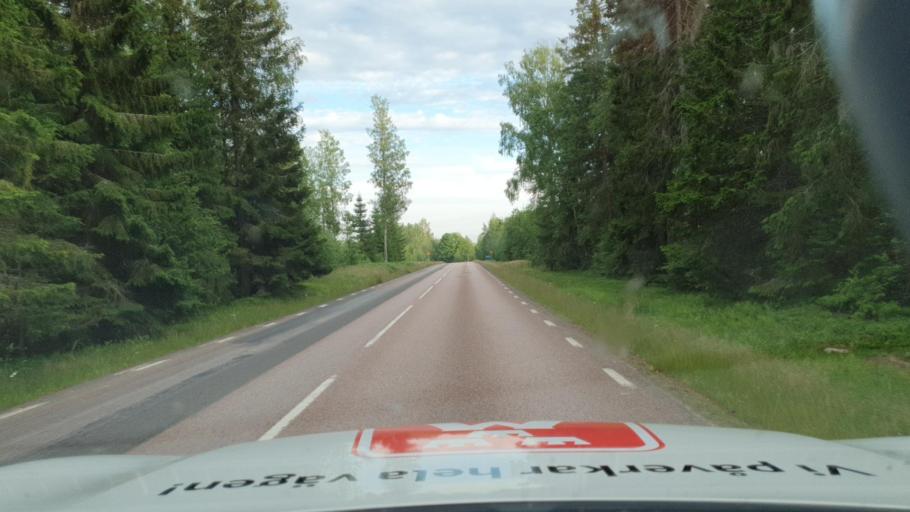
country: SE
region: Vaermland
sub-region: Karlstads Kommun
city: Molkom
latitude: 59.5275
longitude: 13.7901
